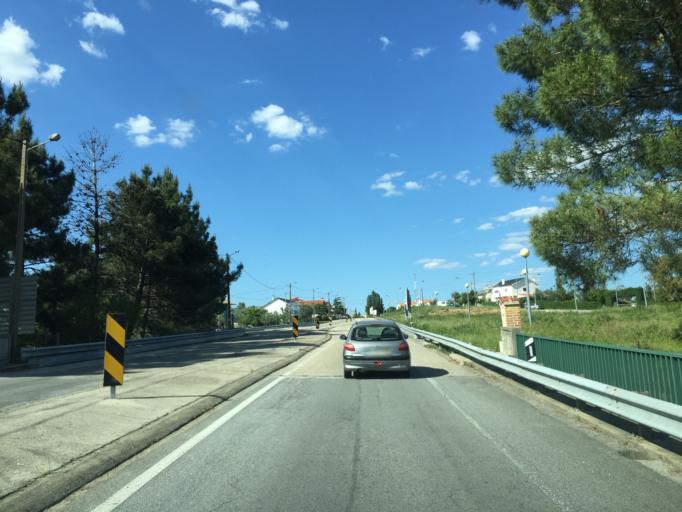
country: PT
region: Leiria
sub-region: Pedrogao Grande
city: Pedrogao Grande
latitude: 39.9097
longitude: -8.1512
